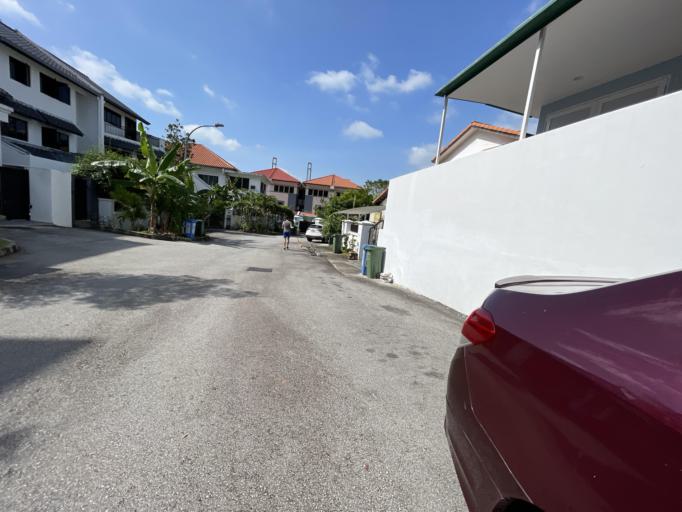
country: SG
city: Singapore
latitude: 1.2798
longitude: 103.7869
